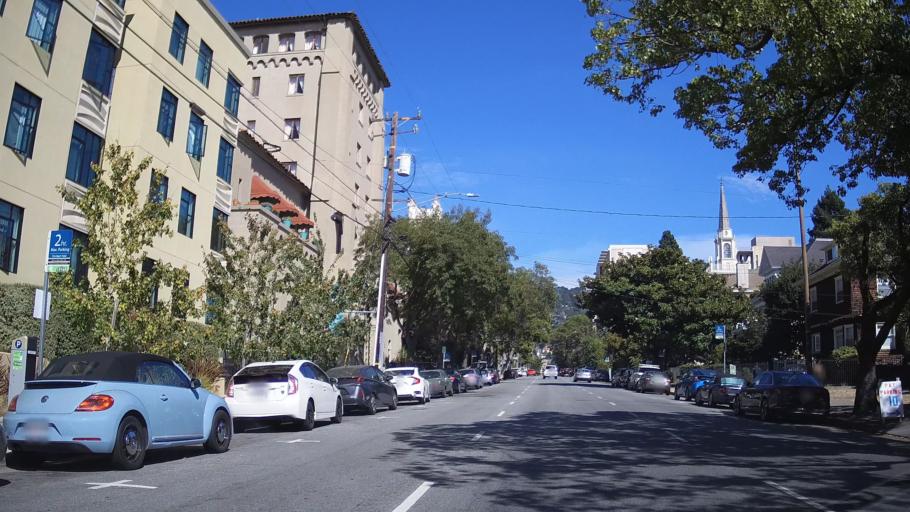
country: US
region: California
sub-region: Alameda County
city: Berkeley
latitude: 37.8672
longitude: -122.2634
